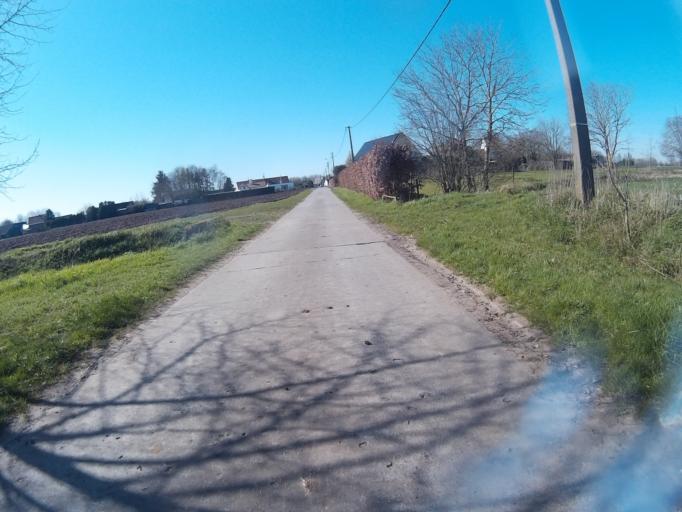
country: BE
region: Flanders
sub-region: Provincie Oost-Vlaanderen
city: Aalter
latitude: 51.1118
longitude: 3.4743
